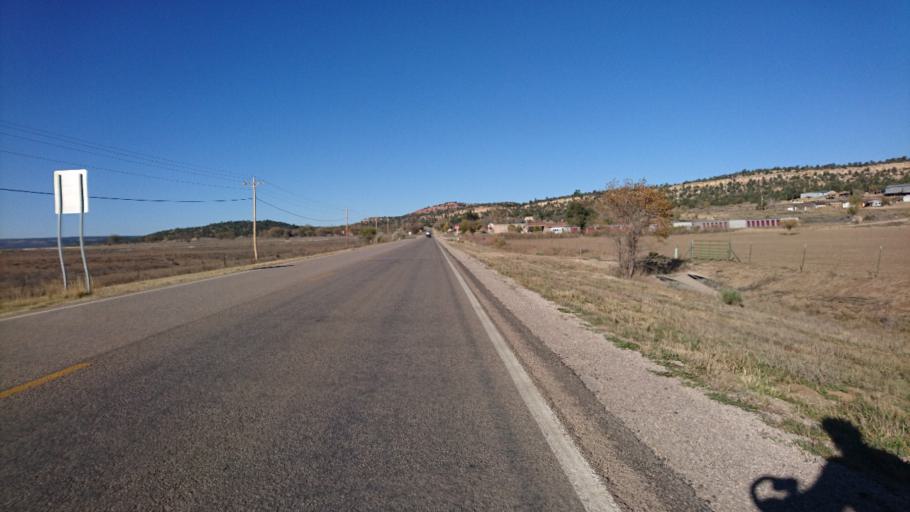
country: US
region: New Mexico
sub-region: McKinley County
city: Black Rock
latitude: 35.1333
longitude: -108.5051
